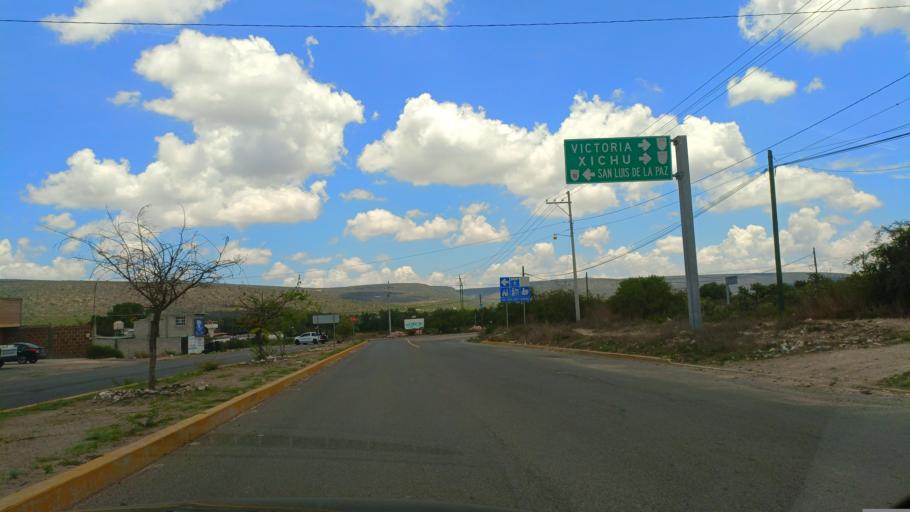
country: MX
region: Guanajuato
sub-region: San Luis de la Paz
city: San Luis de la Paz
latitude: 21.2942
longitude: -100.4899
